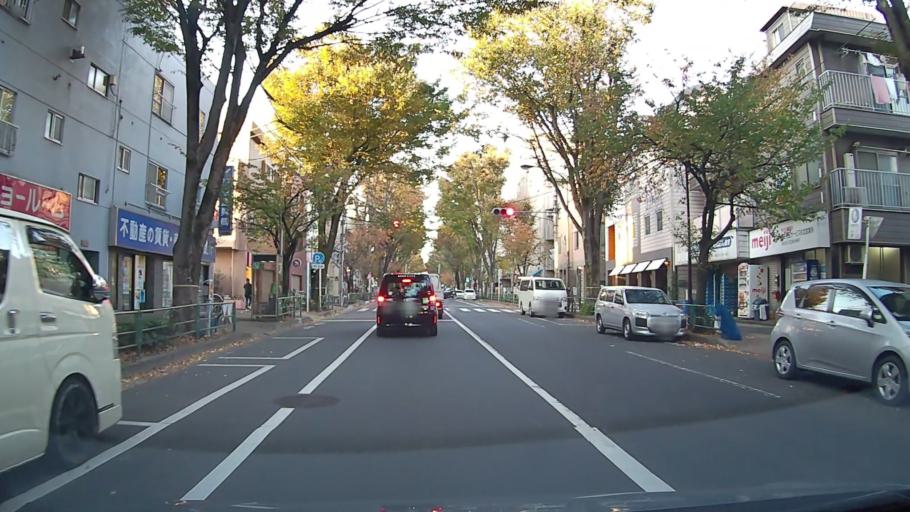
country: JP
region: Tokyo
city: Tokyo
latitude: 35.7110
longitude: 139.6352
